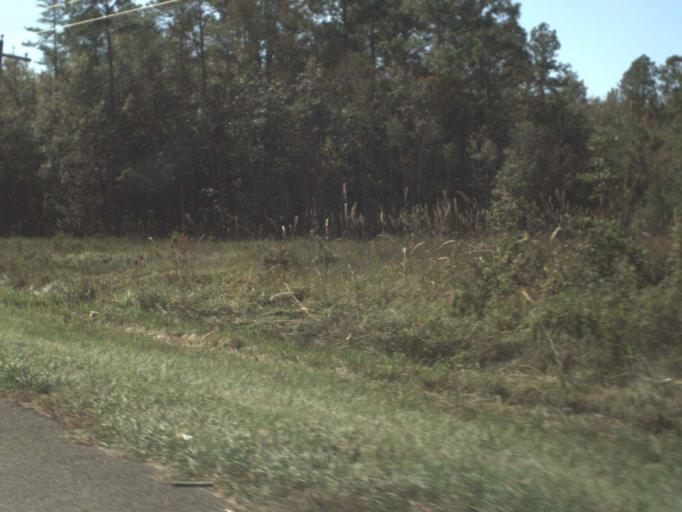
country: US
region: Florida
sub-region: Walton County
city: DeFuniak Springs
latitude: 30.9042
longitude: -86.1313
